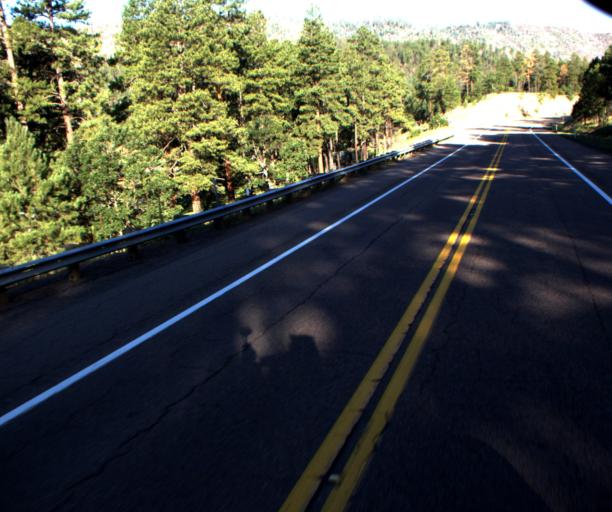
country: US
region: Arizona
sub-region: Apache County
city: Eagar
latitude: 33.9043
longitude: -109.1623
